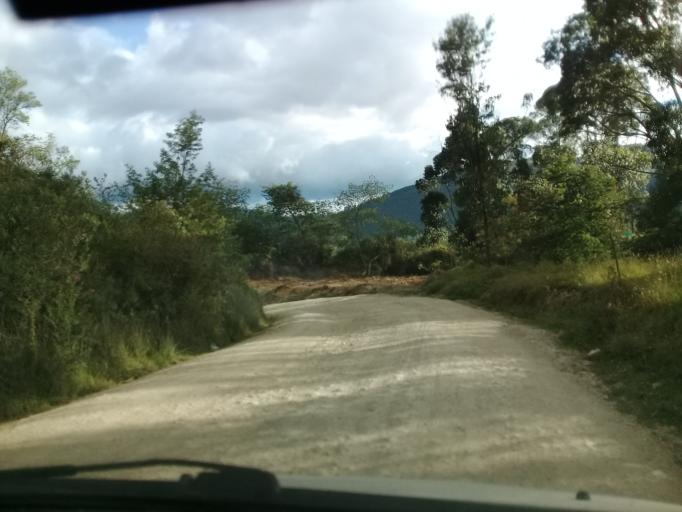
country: CO
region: Cundinamarca
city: Villapinzon
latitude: 5.2243
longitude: -73.6460
